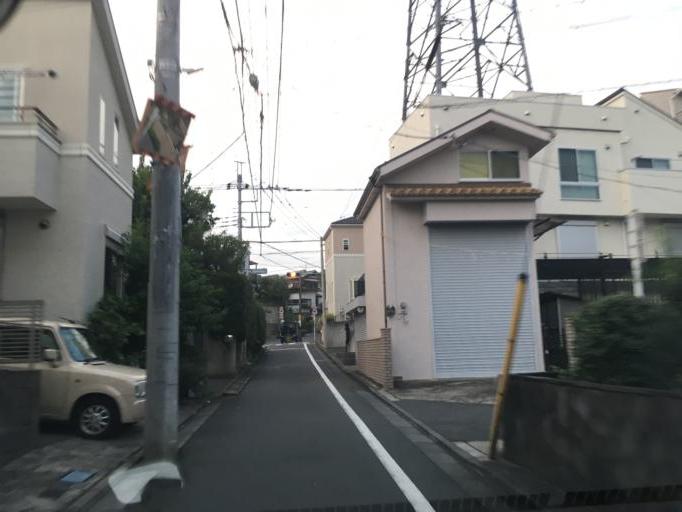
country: JP
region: Tokyo
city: Kokubunji
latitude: 35.6940
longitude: 139.4561
